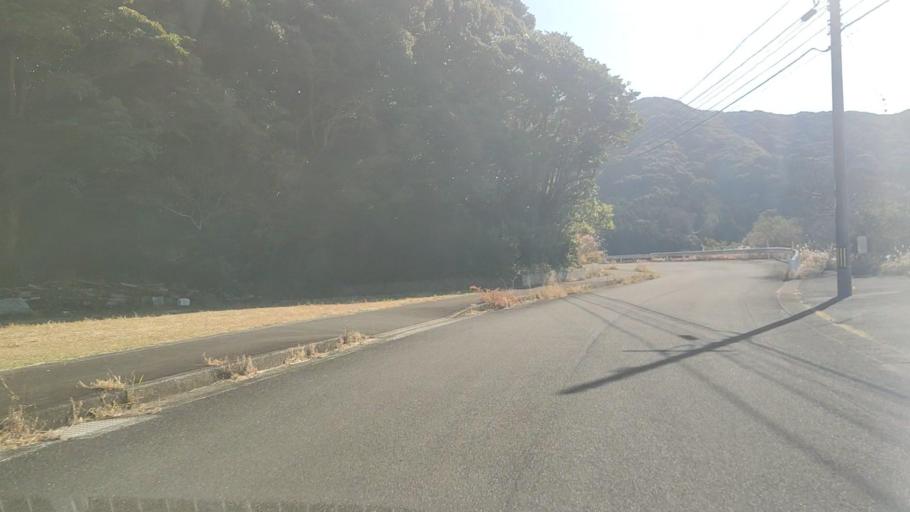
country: JP
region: Oita
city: Saiki
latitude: 32.7959
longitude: 131.8966
